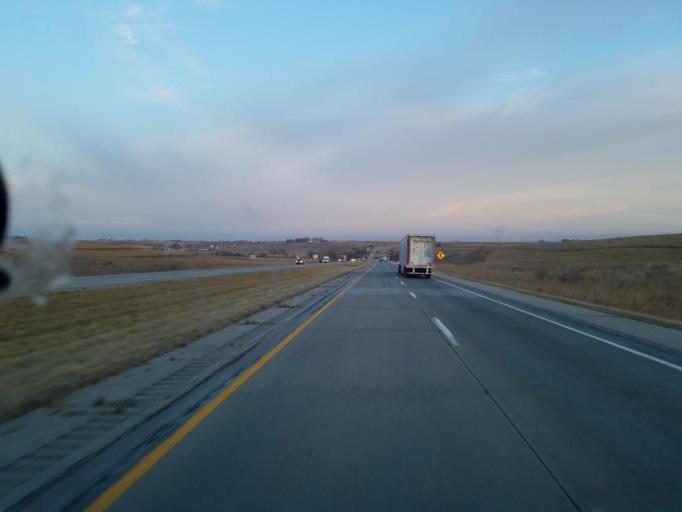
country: US
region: Iowa
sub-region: Pottawattamie County
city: Avoca
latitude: 41.4981
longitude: -95.5443
